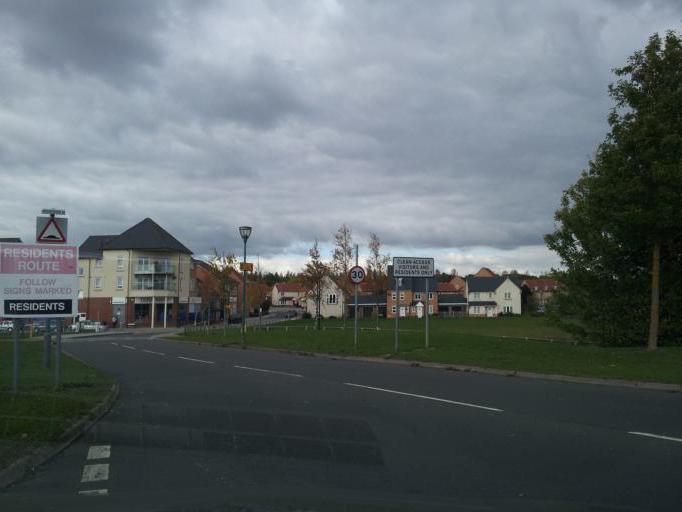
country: GB
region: England
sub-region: Milton Keynes
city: Shenley Church End
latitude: 52.0070
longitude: -0.8022
